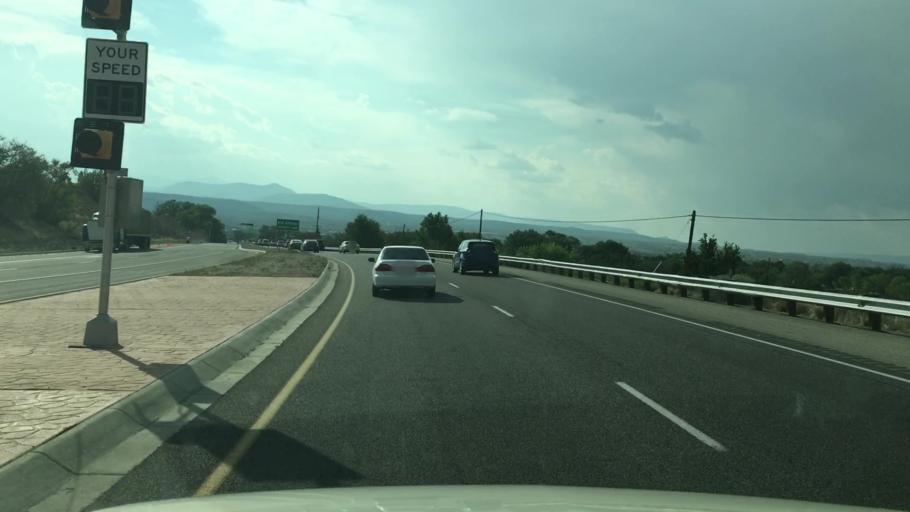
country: US
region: New Mexico
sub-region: Rio Arriba County
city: Espanola
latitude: 35.9858
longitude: -106.0533
